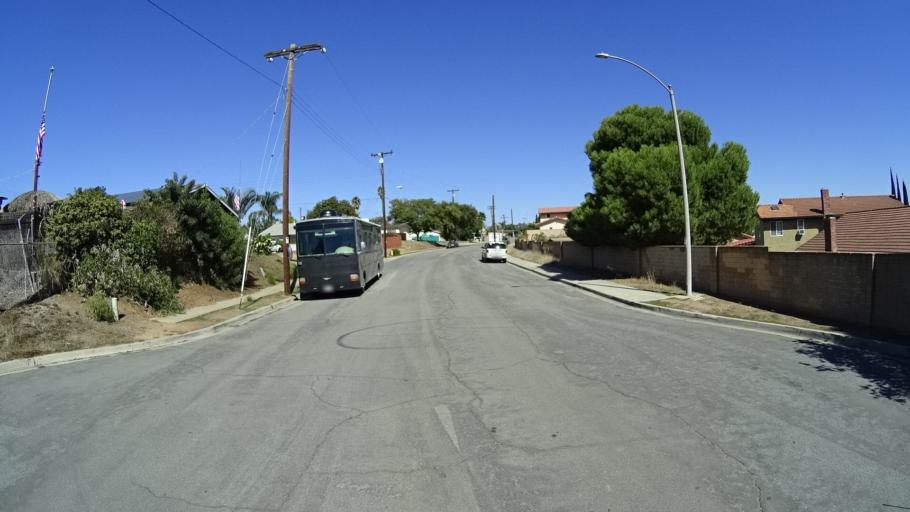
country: US
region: California
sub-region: San Diego County
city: La Presa
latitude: 32.6961
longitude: -117.0065
